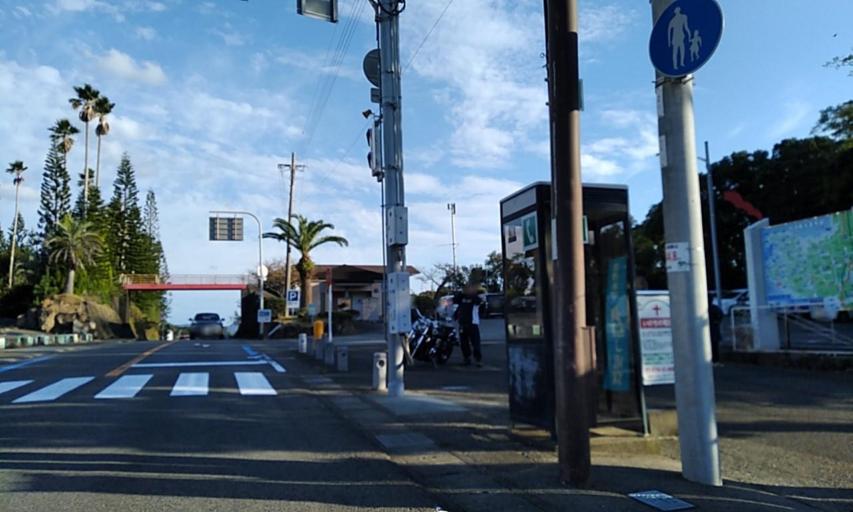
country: JP
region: Wakayama
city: Tanabe
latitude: 33.6663
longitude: 135.3370
